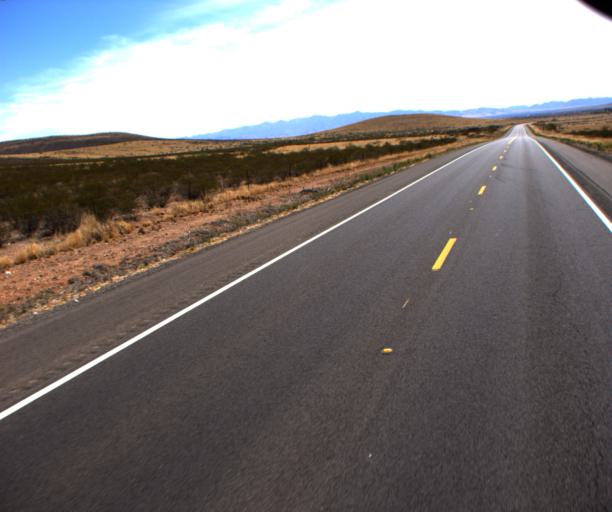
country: US
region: Arizona
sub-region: Cochise County
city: Willcox
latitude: 31.9006
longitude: -109.7088
